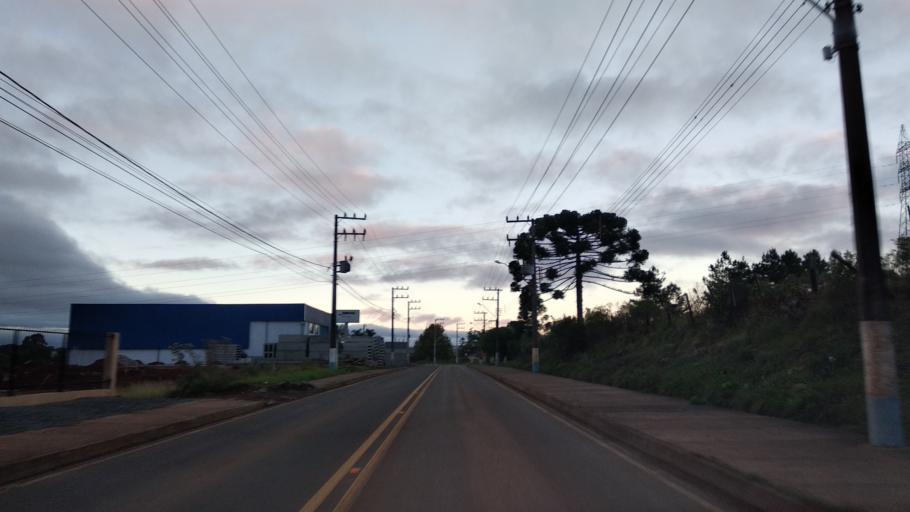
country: BR
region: Santa Catarina
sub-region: Campos Novos
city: Campos Novos
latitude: -27.3816
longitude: -51.2098
